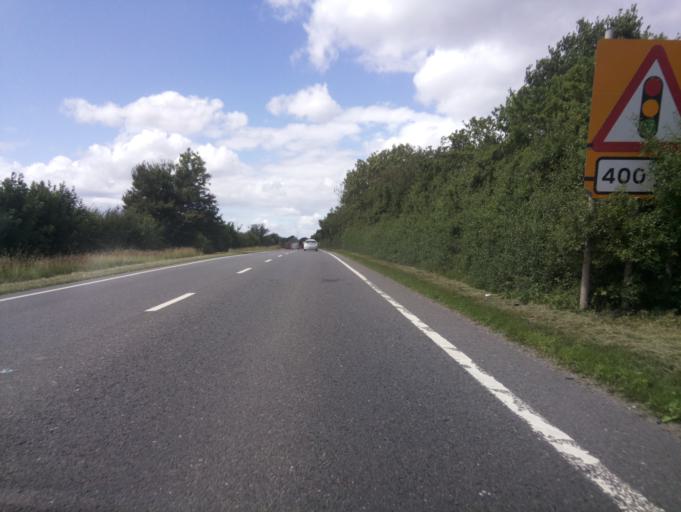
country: GB
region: England
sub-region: Nottinghamshire
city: East Bridgford
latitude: 52.9749
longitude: -0.9701
